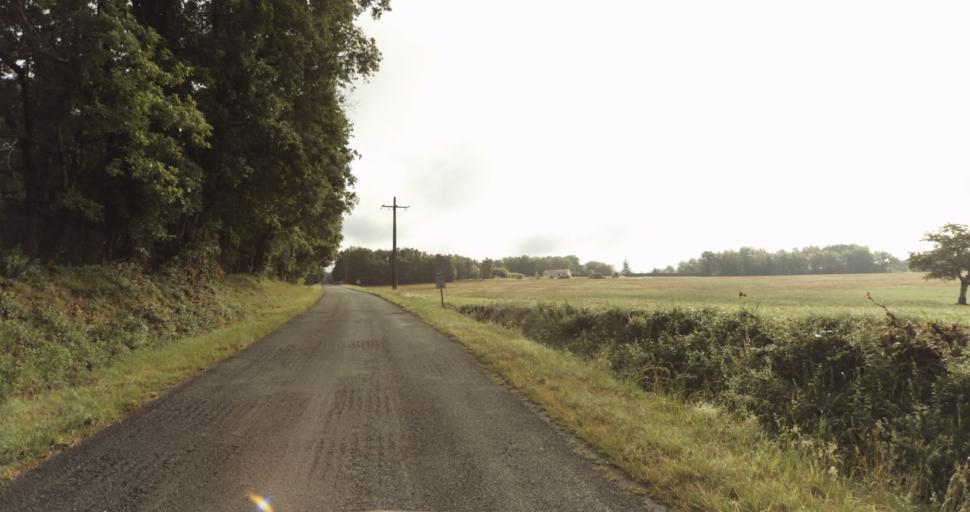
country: FR
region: Aquitaine
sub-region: Departement de la Dordogne
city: Le Bugue
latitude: 44.9201
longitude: 0.8200
